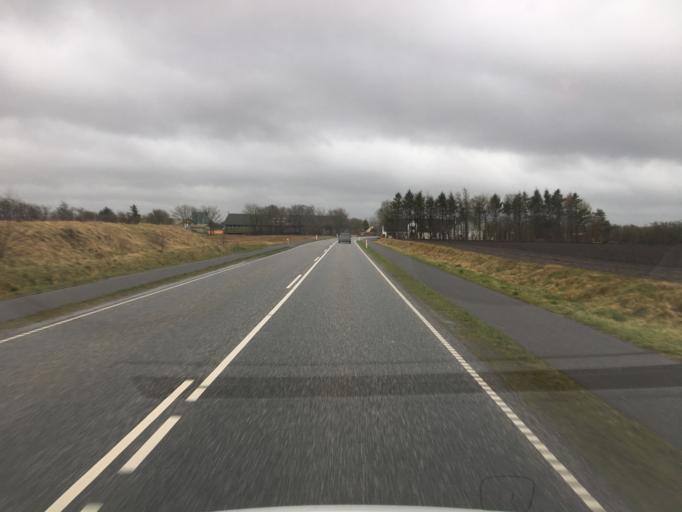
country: DK
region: South Denmark
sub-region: Aabenraa Kommune
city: Tinglev
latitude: 54.9236
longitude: 9.2463
